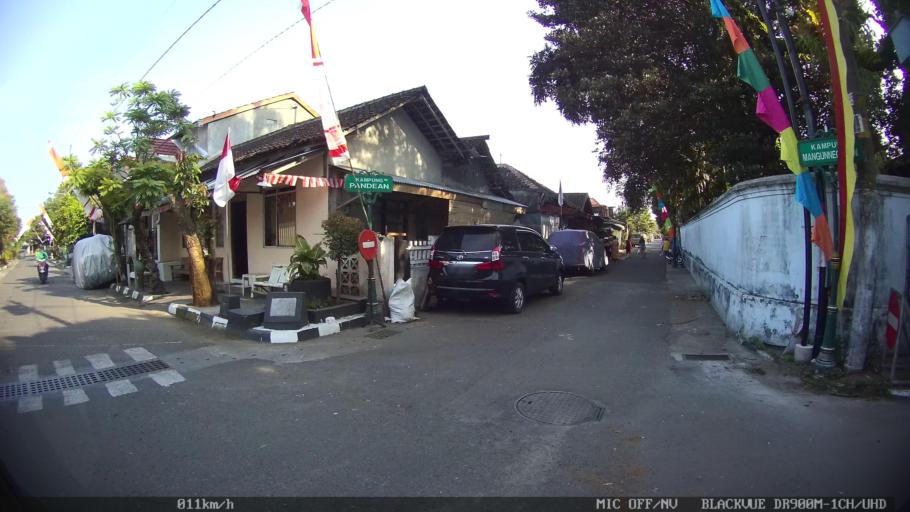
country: ID
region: Daerah Istimewa Yogyakarta
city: Yogyakarta
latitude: -7.8055
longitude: 110.3680
